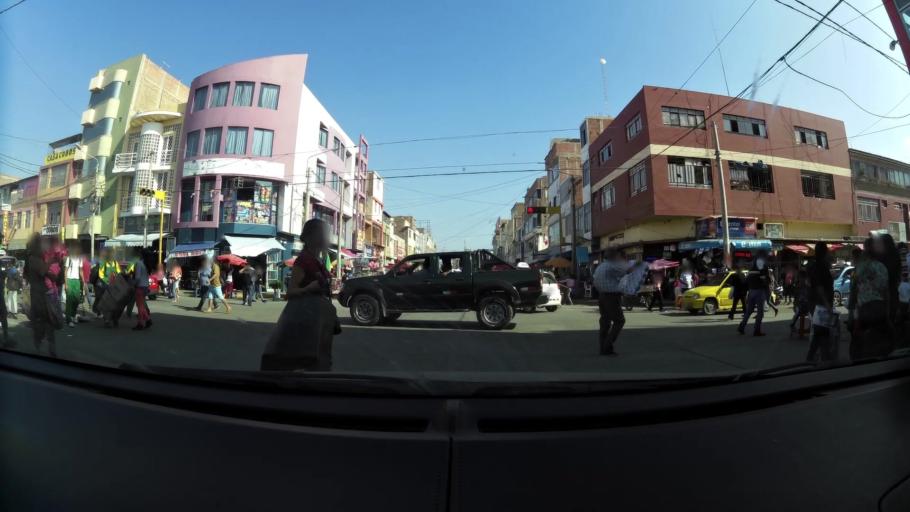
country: PE
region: Lambayeque
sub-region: Provincia de Chiclayo
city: Chiclayo
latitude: -6.7664
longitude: -79.8403
